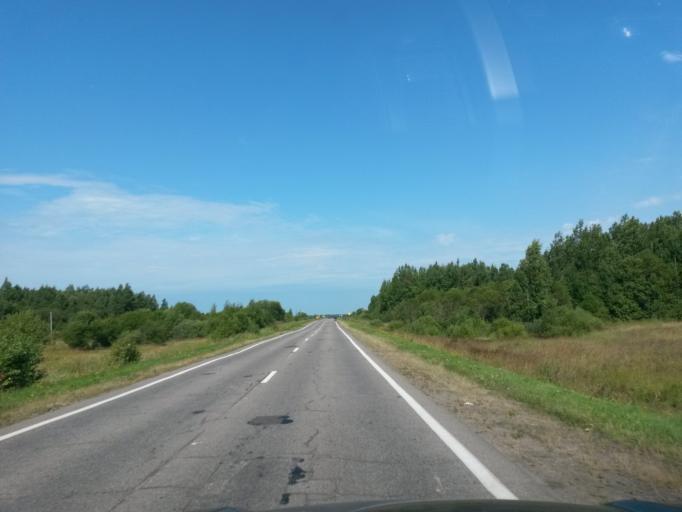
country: RU
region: Jaroslavl
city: Konstantinovskiy
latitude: 57.8664
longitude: 39.6056
